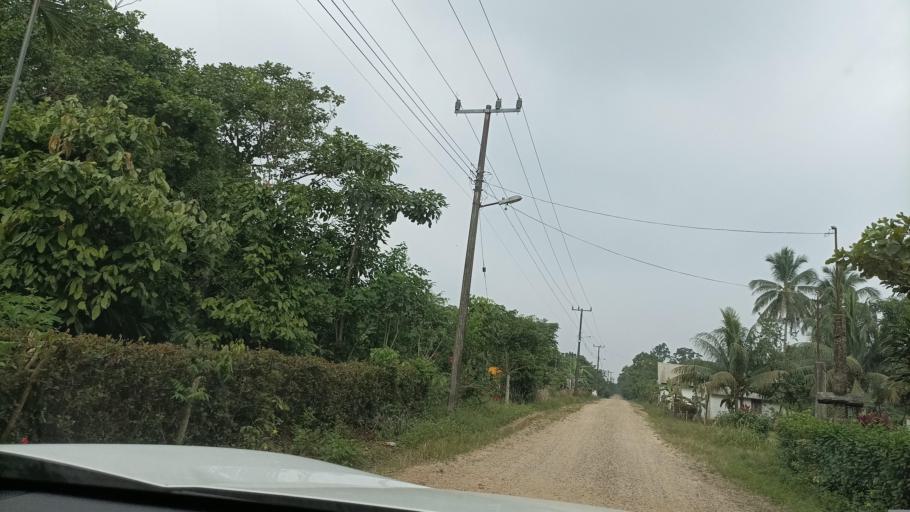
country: MX
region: Veracruz
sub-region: Uxpanapa
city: Poblado 10
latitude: 17.5504
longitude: -94.2242
